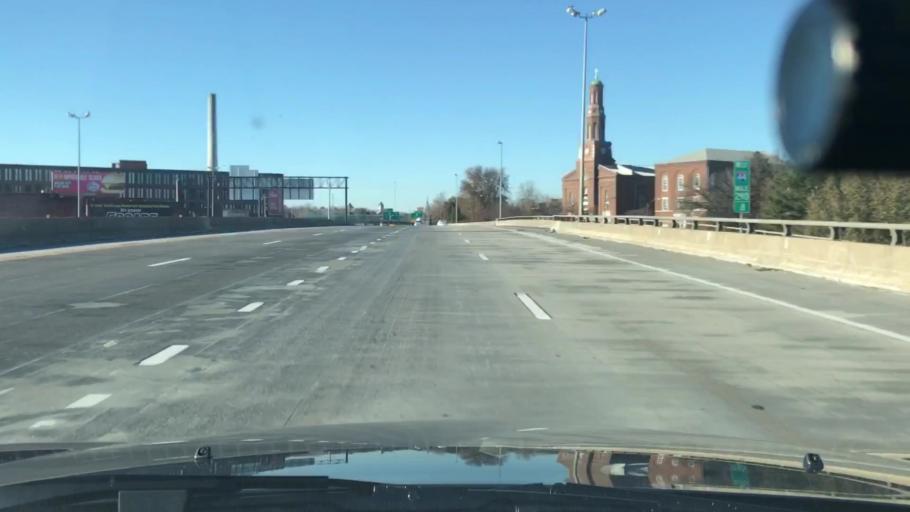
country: US
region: Missouri
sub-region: City of Saint Louis
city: St. Louis
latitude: 38.6136
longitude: -90.1984
